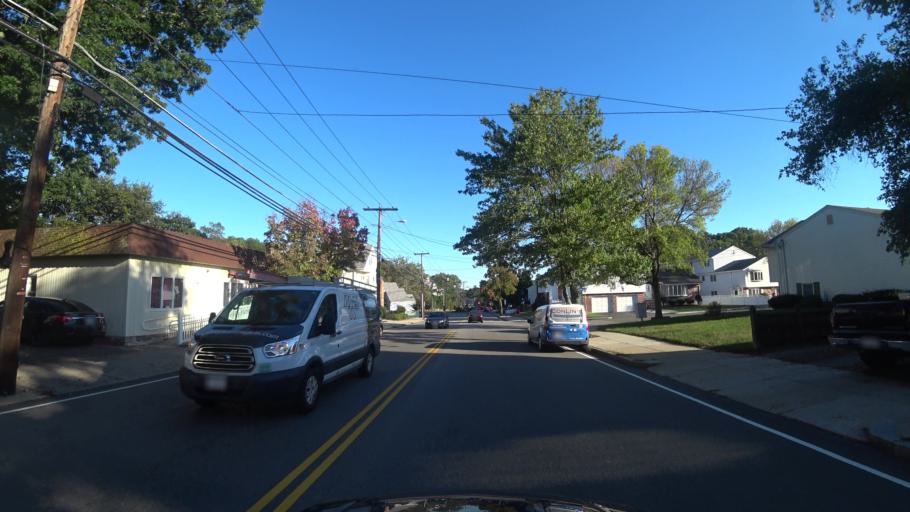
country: US
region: Massachusetts
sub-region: Middlesex County
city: Malden
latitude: 42.4352
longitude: -71.0849
